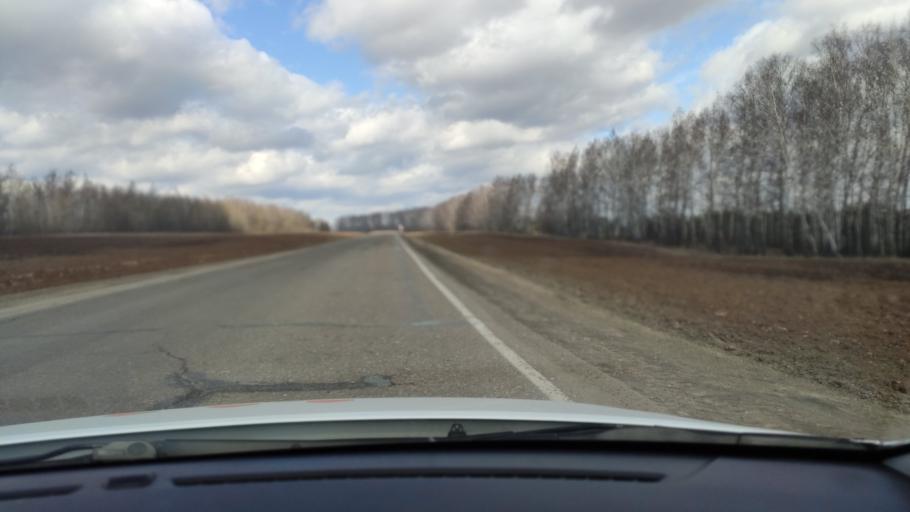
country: RU
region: Tatarstan
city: Vysokaya Gora
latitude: 56.0966
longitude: 49.1835
